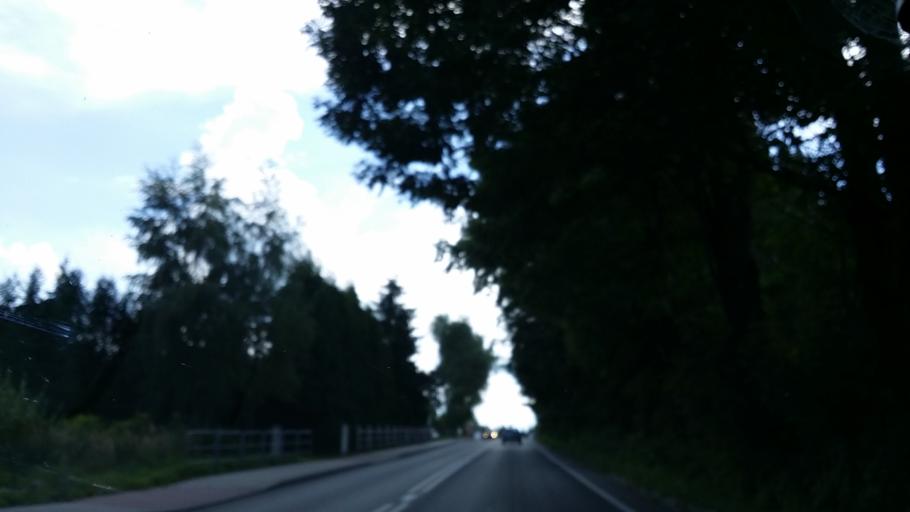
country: PL
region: Lesser Poland Voivodeship
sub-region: Powiat wielicki
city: Wieliczka
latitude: 49.9743
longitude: 20.0633
